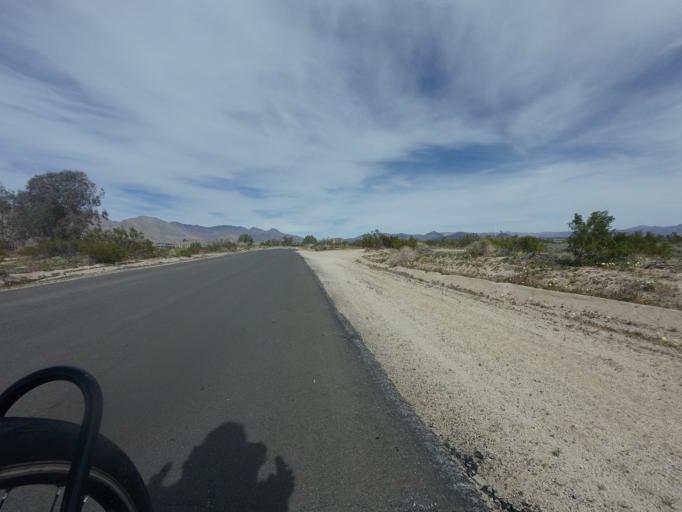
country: US
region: California
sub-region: Kern County
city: Inyokern
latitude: 35.7724
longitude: -117.8499
